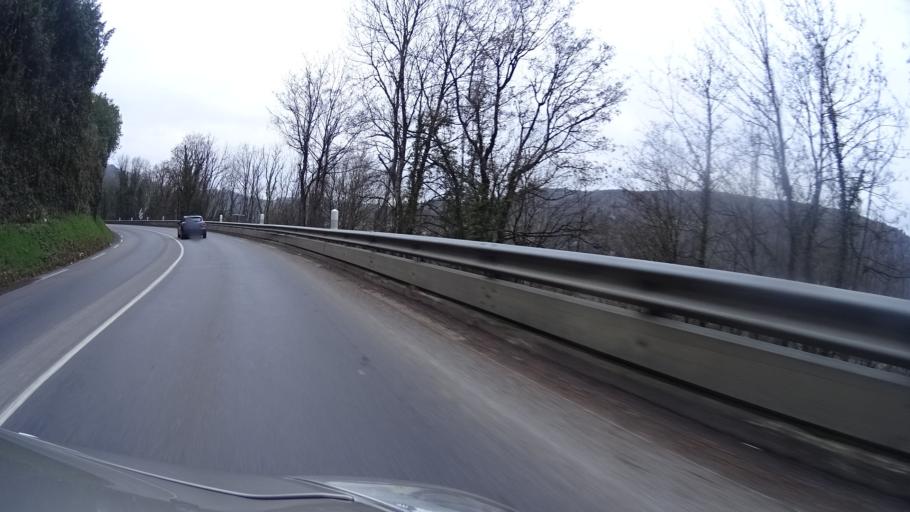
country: FR
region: Franche-Comte
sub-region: Departement du Doubs
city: Morre
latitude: 47.2304
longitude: 6.0608
